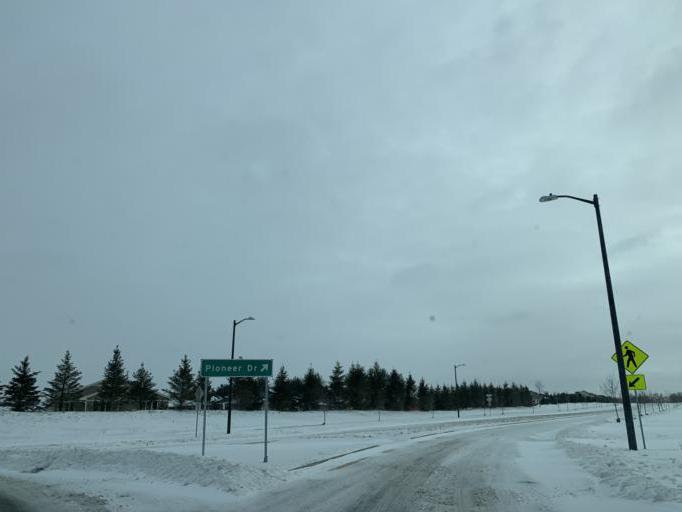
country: US
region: Minnesota
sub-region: Washington County
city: Cottage Grove
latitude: 44.8762
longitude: -92.9239
